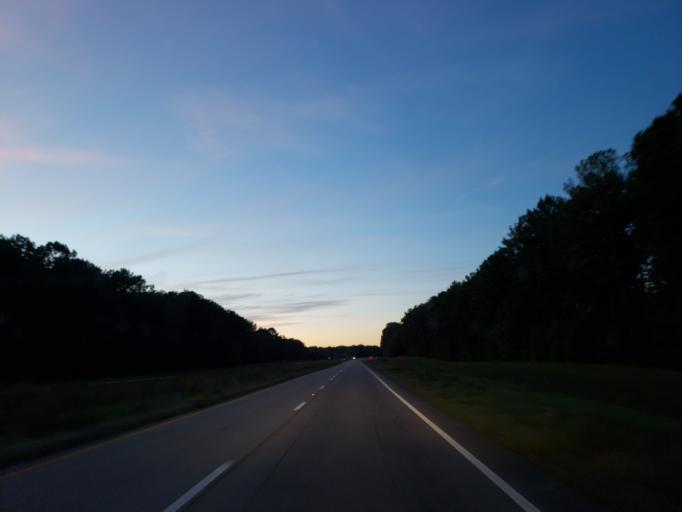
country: US
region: Mississippi
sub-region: Wayne County
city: Waynesboro
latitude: 31.8447
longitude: -88.7113
